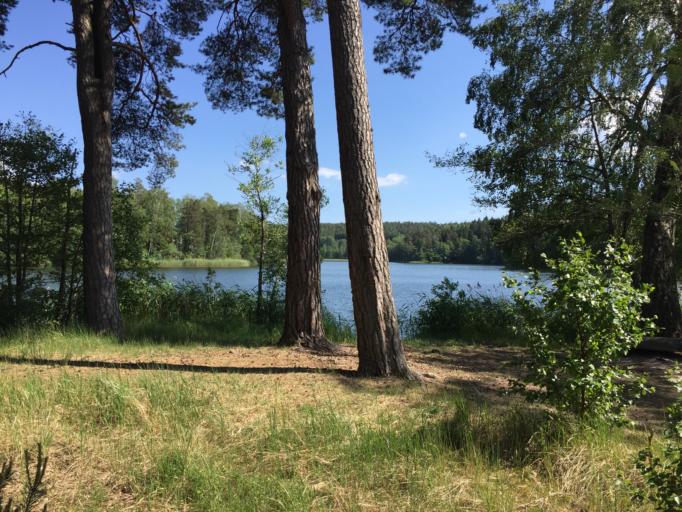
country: SE
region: Stockholm
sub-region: Botkyrka Kommun
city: Varsta
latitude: 59.1606
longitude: 17.7996
